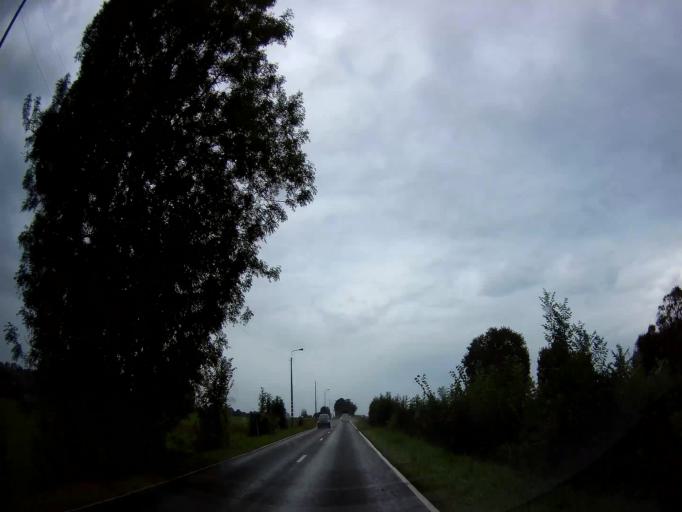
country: BE
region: Wallonia
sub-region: Province de Liege
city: Aywaille
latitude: 50.5100
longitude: 5.7282
